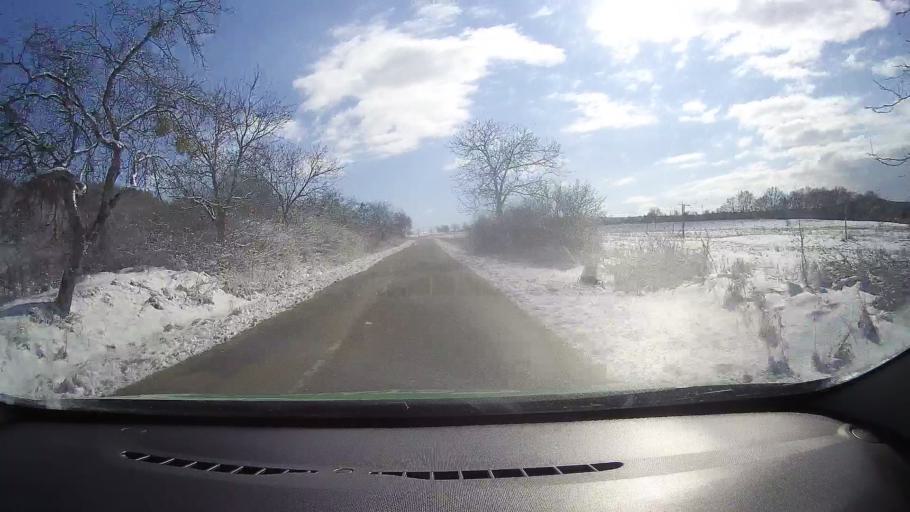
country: RO
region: Sibiu
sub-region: Comuna Mihaileni
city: Mihaileni
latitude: 46.0065
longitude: 24.4251
